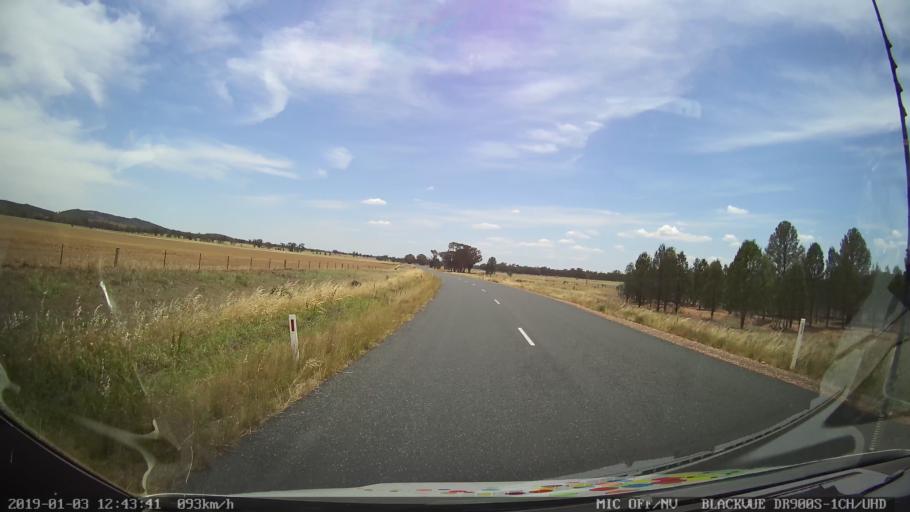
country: AU
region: New South Wales
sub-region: Weddin
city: Grenfell
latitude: -33.7719
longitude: 148.2139
